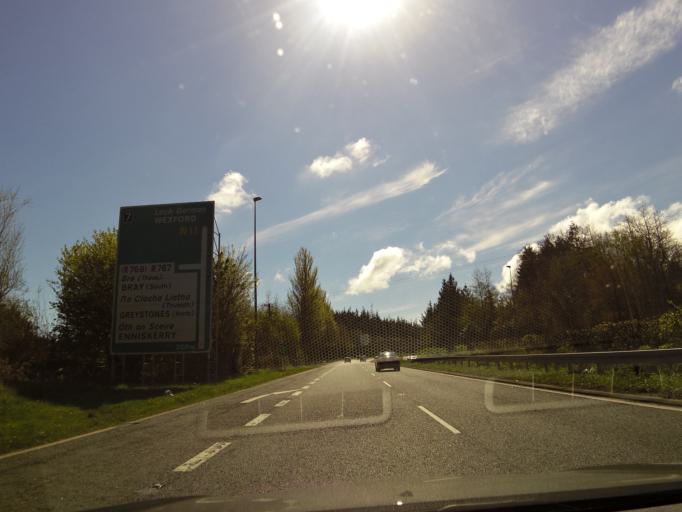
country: IE
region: Leinster
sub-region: Wicklow
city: Kilmacanoge
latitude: 53.1866
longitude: -6.1365
